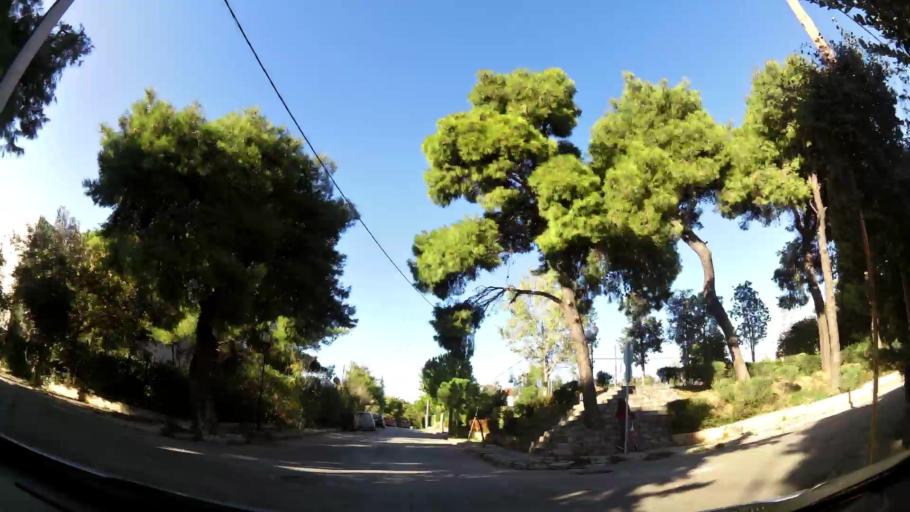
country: GR
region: Attica
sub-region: Nomarchia Athinas
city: Kifisia
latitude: 38.0855
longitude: 23.8074
